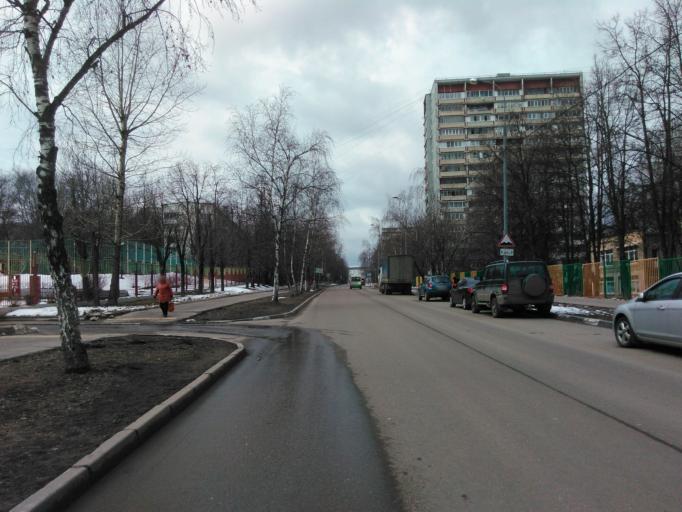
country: RU
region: Moscow
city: Zyuzino
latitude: 55.6506
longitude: 37.5739
